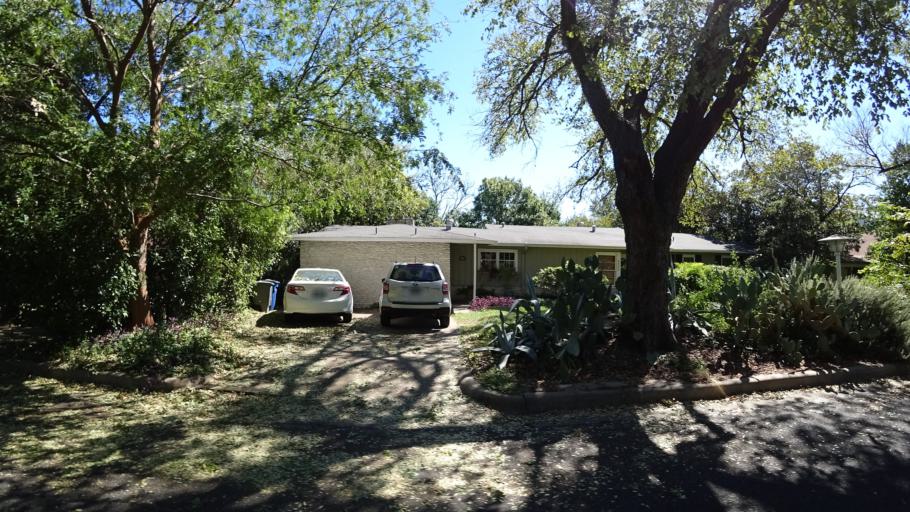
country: US
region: Texas
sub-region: Travis County
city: Austin
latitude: 30.2391
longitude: -97.7433
